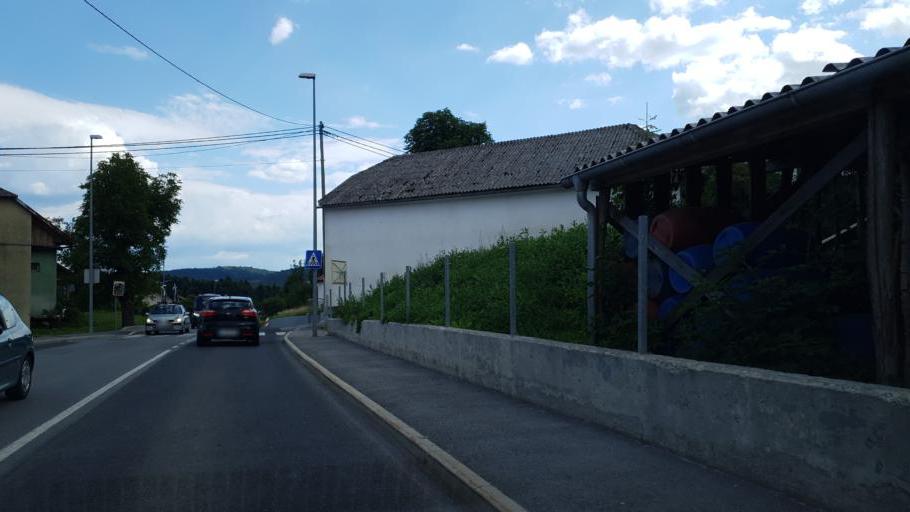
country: SI
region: Pivka
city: Pivka
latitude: 45.6561
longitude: 14.2219
